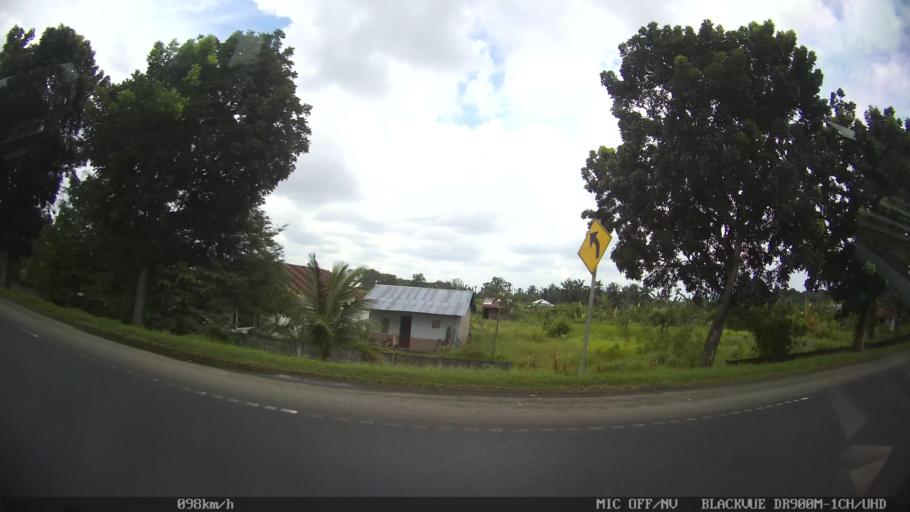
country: ID
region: North Sumatra
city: Medan
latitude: 3.6246
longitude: 98.7195
